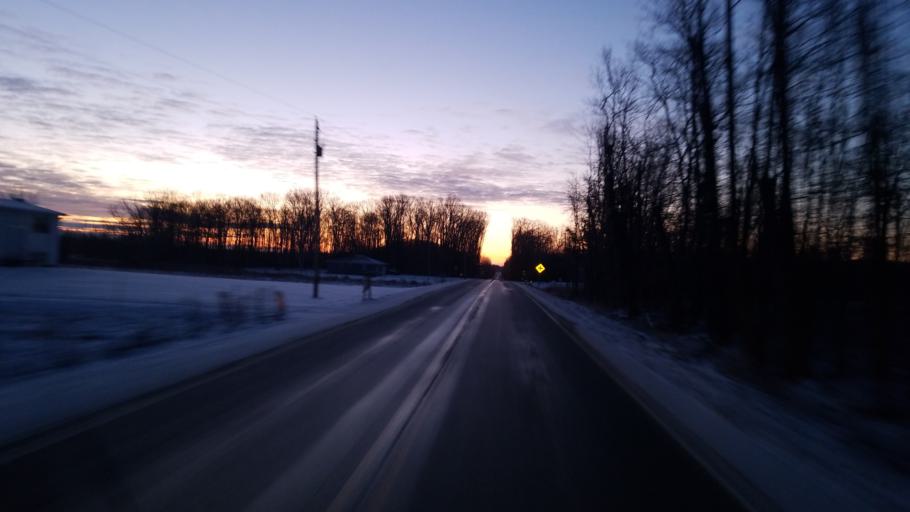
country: US
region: Pennsylvania
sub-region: Clarion County
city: Knox
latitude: 41.2730
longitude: -79.5707
